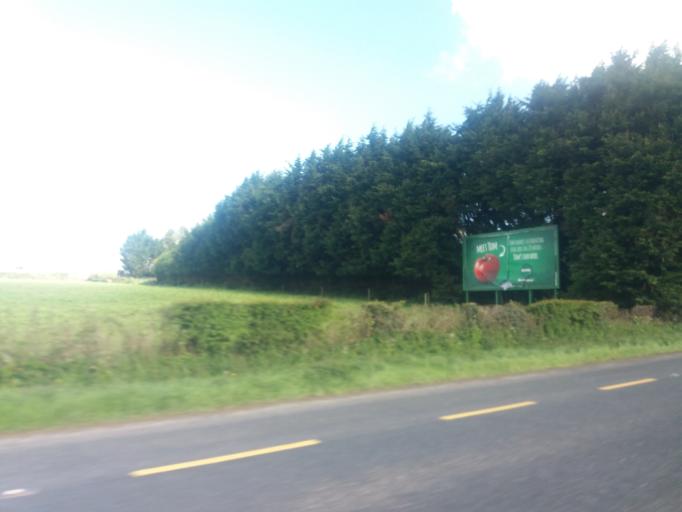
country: IE
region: Leinster
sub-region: Loch Garman
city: Ferns
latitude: 52.5644
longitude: -6.5273
